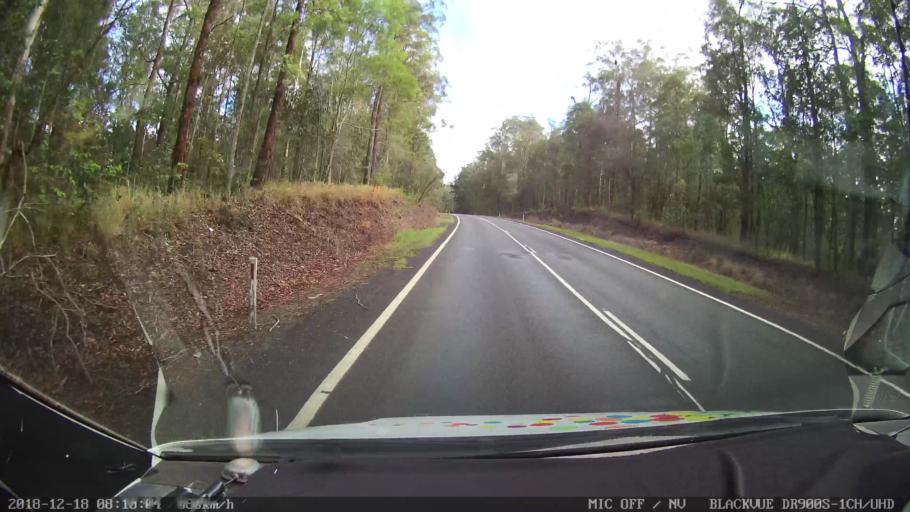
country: AU
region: New South Wales
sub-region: Kyogle
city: Kyogle
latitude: -28.3656
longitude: 152.6598
